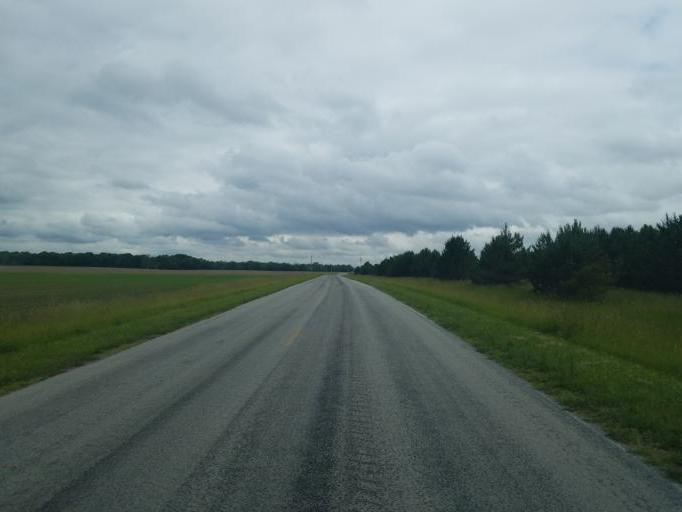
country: US
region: Ohio
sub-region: Wyandot County
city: Upper Sandusky
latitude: 40.7302
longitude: -83.1983
